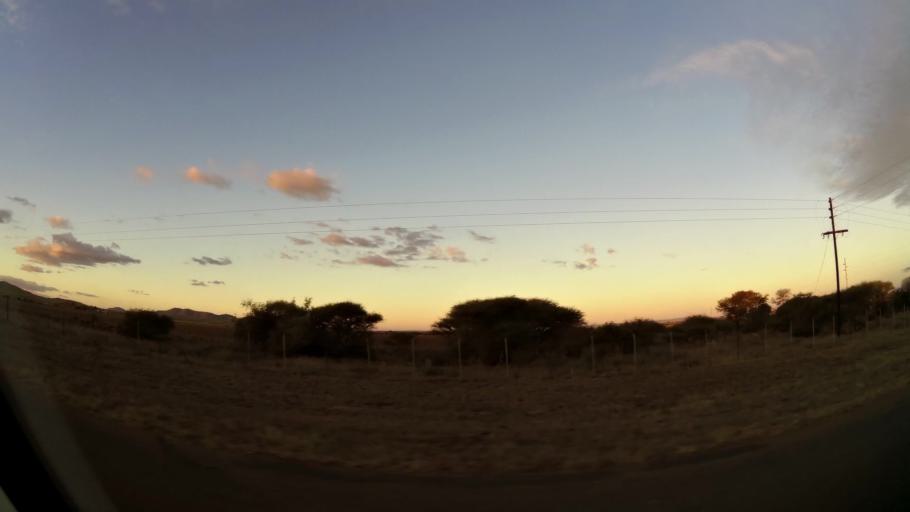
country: ZA
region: Limpopo
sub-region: Capricorn District Municipality
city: Polokwane
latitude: -23.7487
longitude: 29.4714
